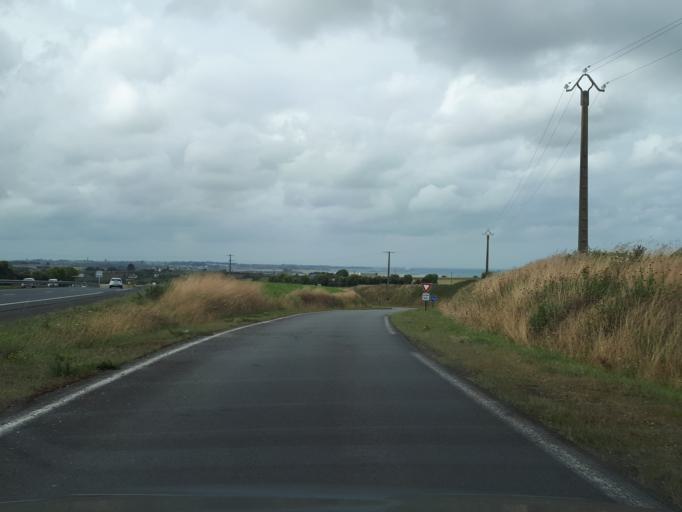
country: FR
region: Brittany
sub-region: Departement du Finistere
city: Henvic
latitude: 48.6350
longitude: -3.9234
